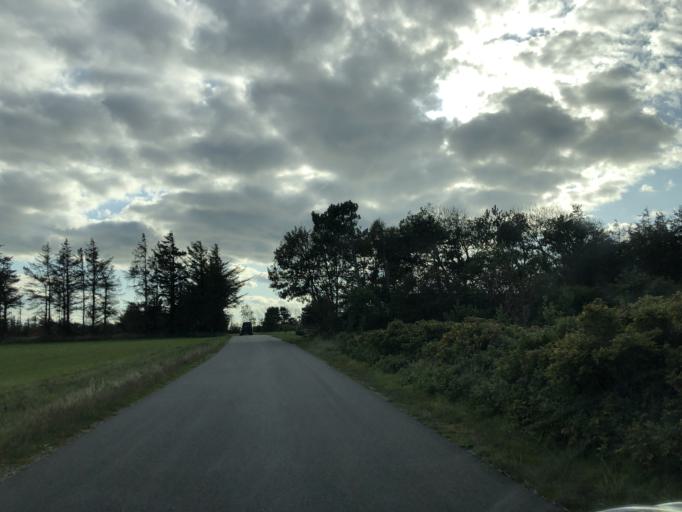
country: DK
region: Central Jutland
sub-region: Holstebro Kommune
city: Ulfborg
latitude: 56.3266
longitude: 8.1581
